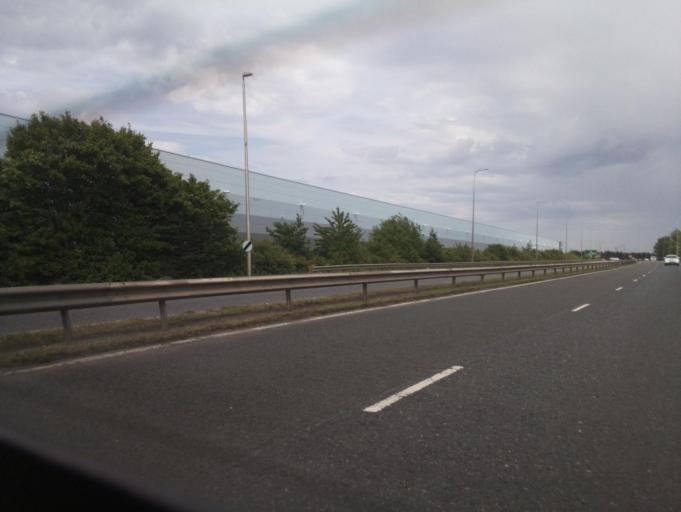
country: GB
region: England
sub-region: South Tyneside
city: The Boldons
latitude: 54.9075
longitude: -1.4711
